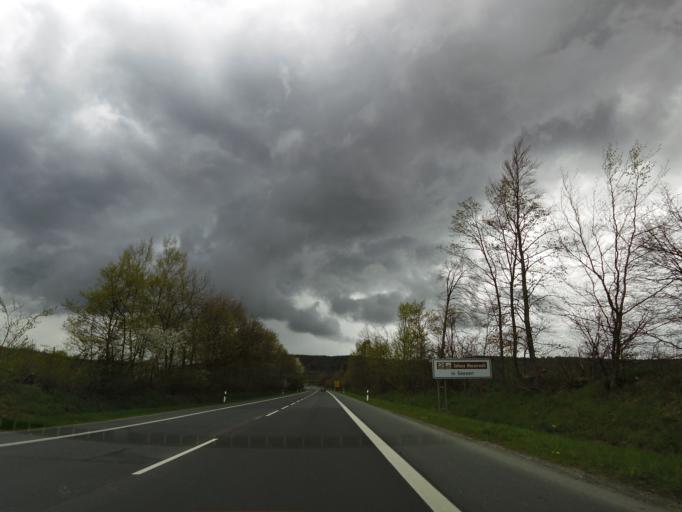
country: DE
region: Lower Saxony
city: Hahausen
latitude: 51.9560
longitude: 10.2412
